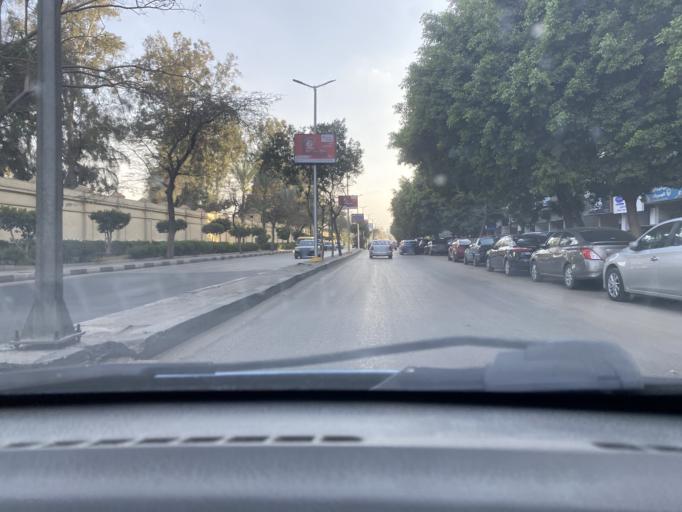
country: EG
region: Muhafazat al Qahirah
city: Cairo
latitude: 30.1005
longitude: 31.3002
